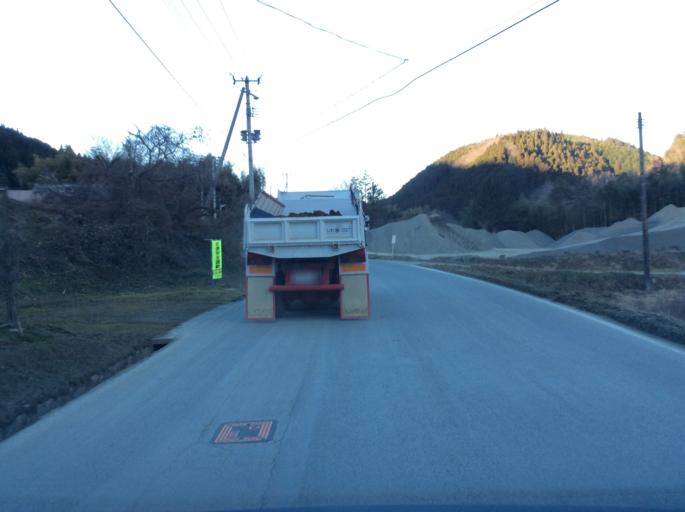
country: JP
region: Ibaraki
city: Kitaibaraki
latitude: 36.8812
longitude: 140.7222
